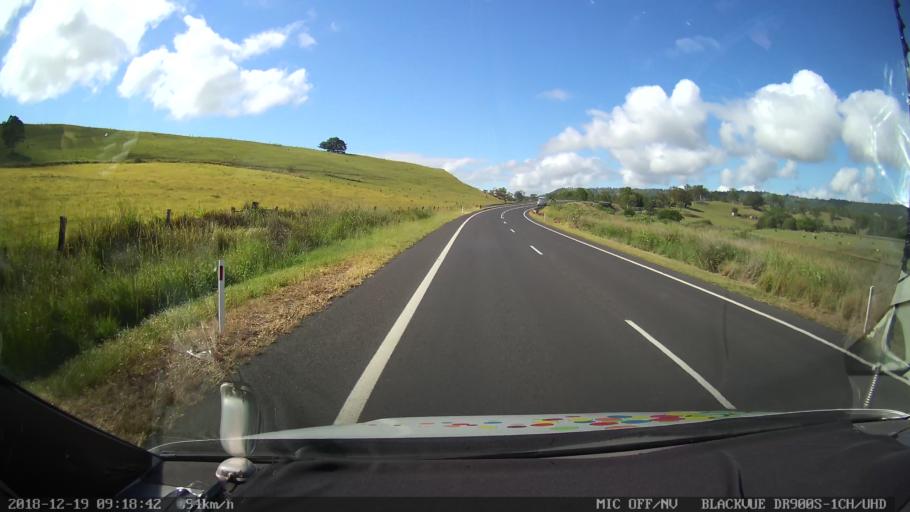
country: AU
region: New South Wales
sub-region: Kyogle
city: Kyogle
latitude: -28.5510
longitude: 152.9766
